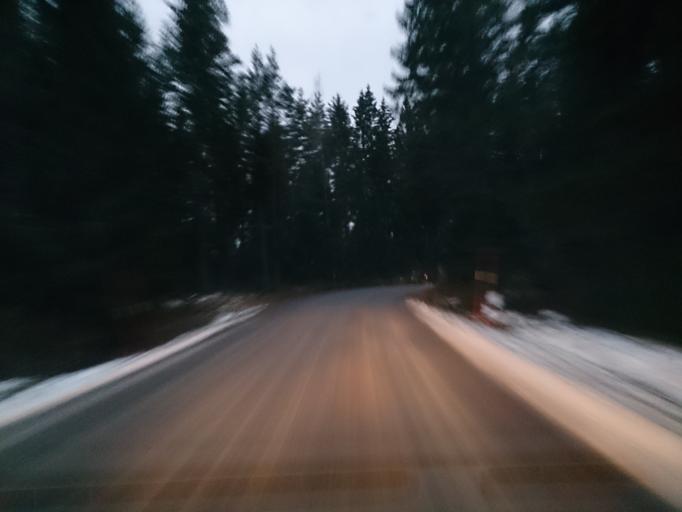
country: SE
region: OEstergoetland
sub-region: Atvidabergs Kommun
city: Atvidaberg
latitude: 58.2255
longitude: 16.0553
